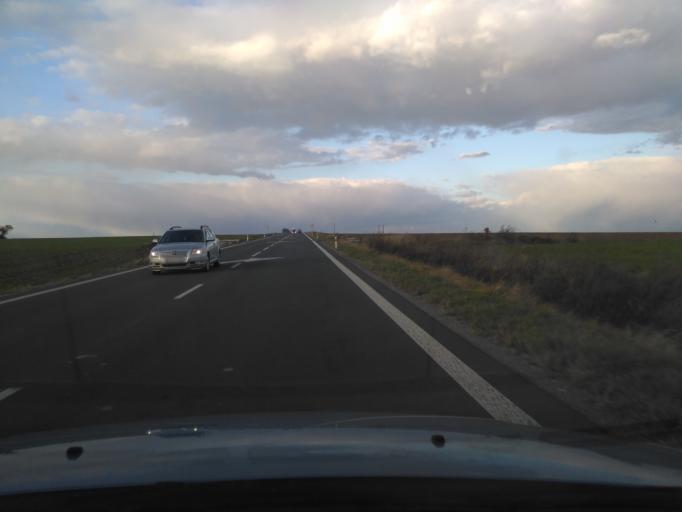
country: SK
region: Kosicky
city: Trebisov
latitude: 48.5694
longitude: 21.7015
